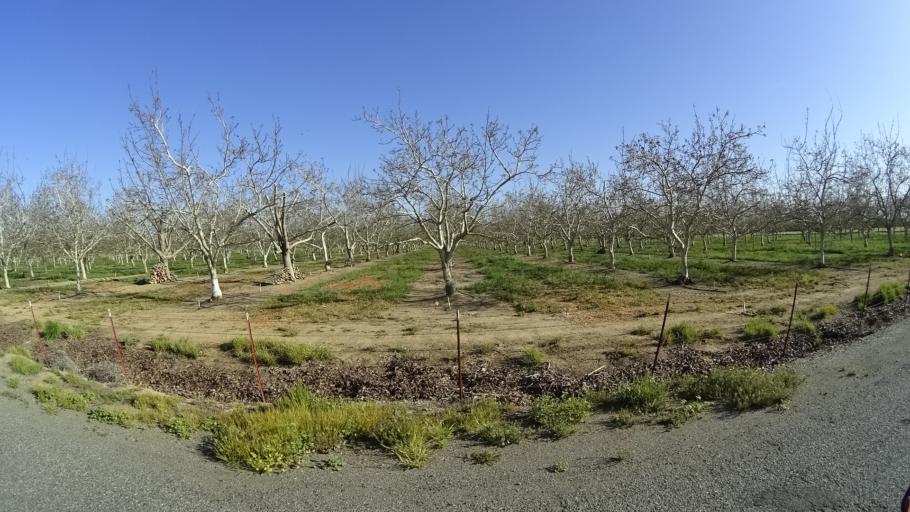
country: US
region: California
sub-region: Glenn County
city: Orland
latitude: 39.6820
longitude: -122.1700
